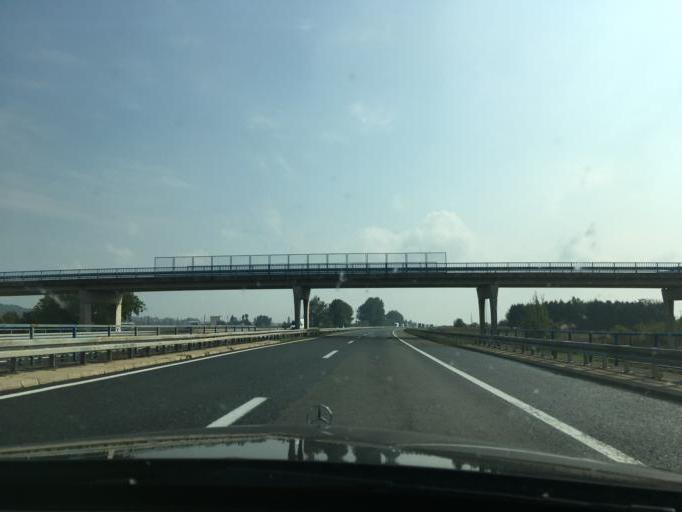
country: HR
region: Brodsko-Posavska
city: Podvinje
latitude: 45.1844
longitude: 18.0310
